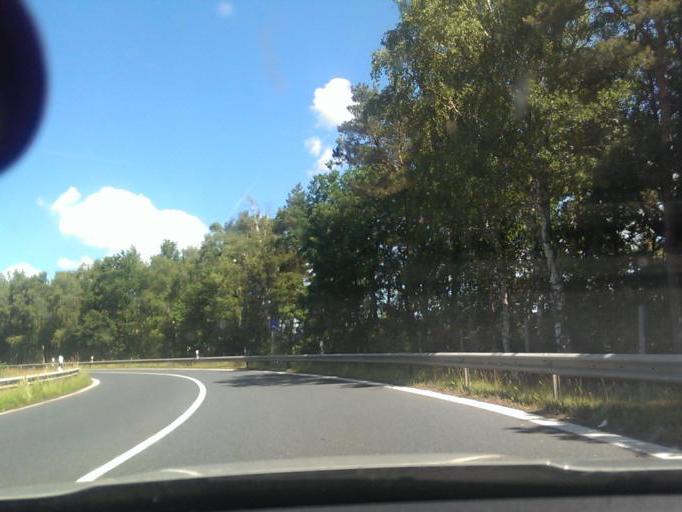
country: DE
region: Lower Saxony
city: Verden
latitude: 52.9593
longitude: 9.2470
